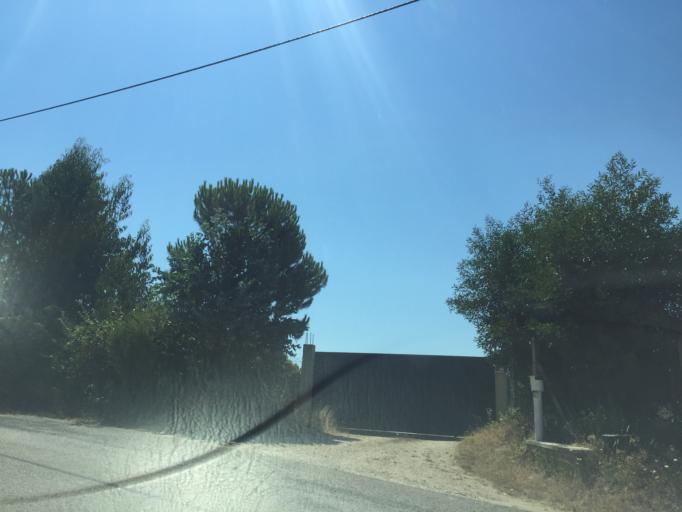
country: PT
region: Santarem
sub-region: Ferreira do Zezere
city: Ferreira do Zezere
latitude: 39.6404
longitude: -8.3398
